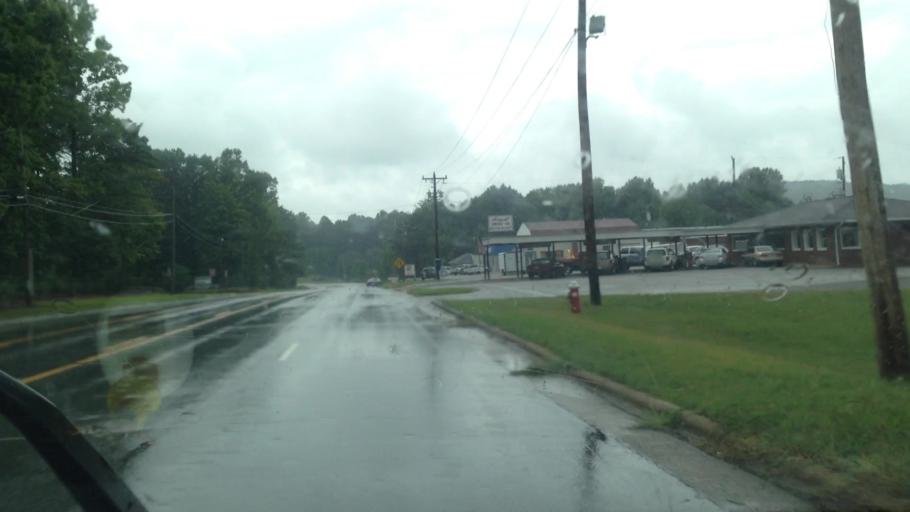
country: US
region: North Carolina
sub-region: Rockingham County
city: Mayodan
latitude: 36.4030
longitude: -79.9765
